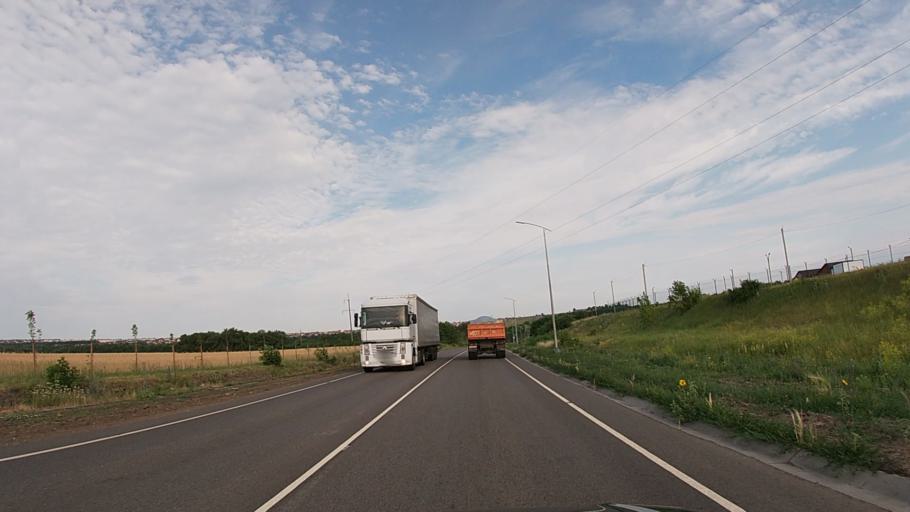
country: RU
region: Belgorod
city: Severnyy
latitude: 50.6660
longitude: 36.4971
